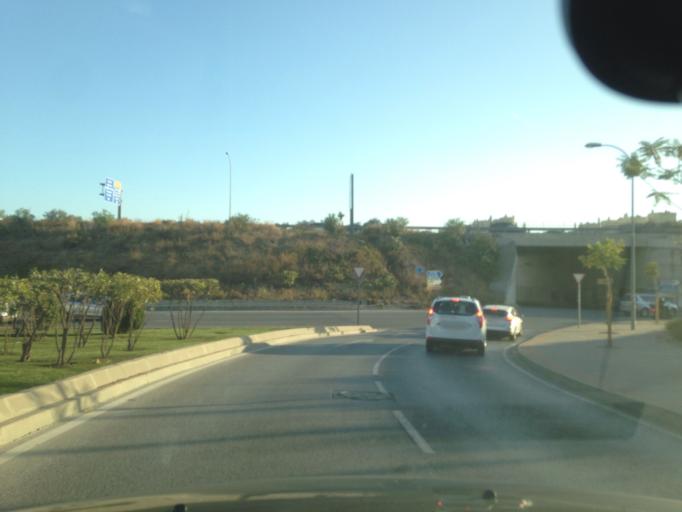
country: ES
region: Andalusia
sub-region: Provincia de Malaga
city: Malaga
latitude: 36.7134
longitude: -4.4630
